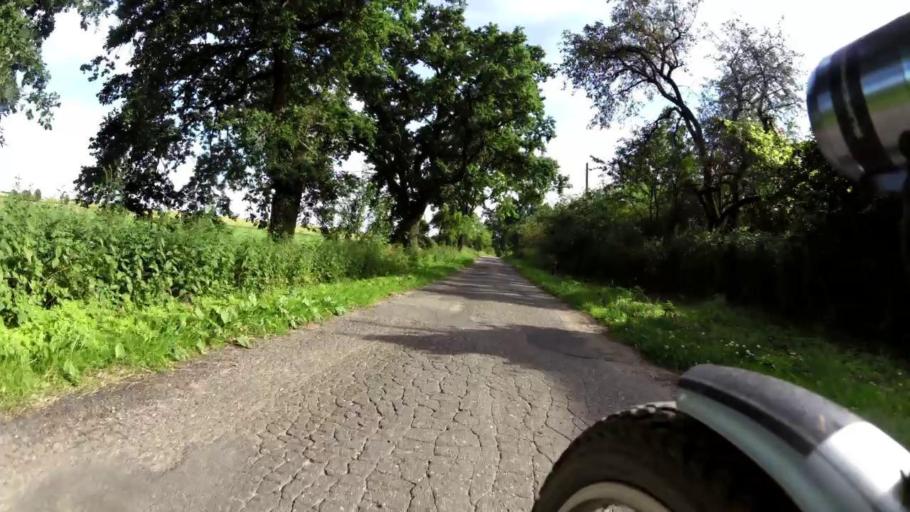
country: PL
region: West Pomeranian Voivodeship
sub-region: Powiat lobeski
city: Radowo Male
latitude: 53.5726
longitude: 15.4688
